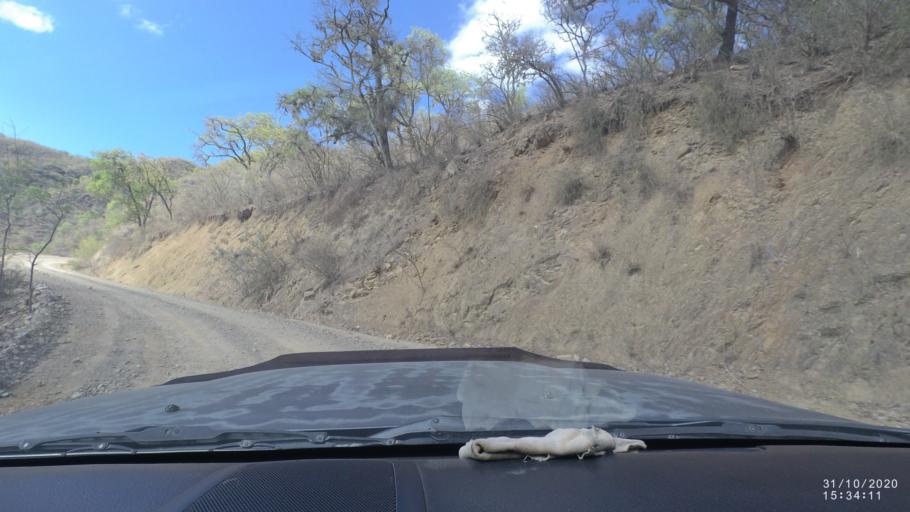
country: BO
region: Chuquisaca
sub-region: Provincia Zudanez
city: Mojocoya
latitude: -18.3429
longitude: -64.7549
